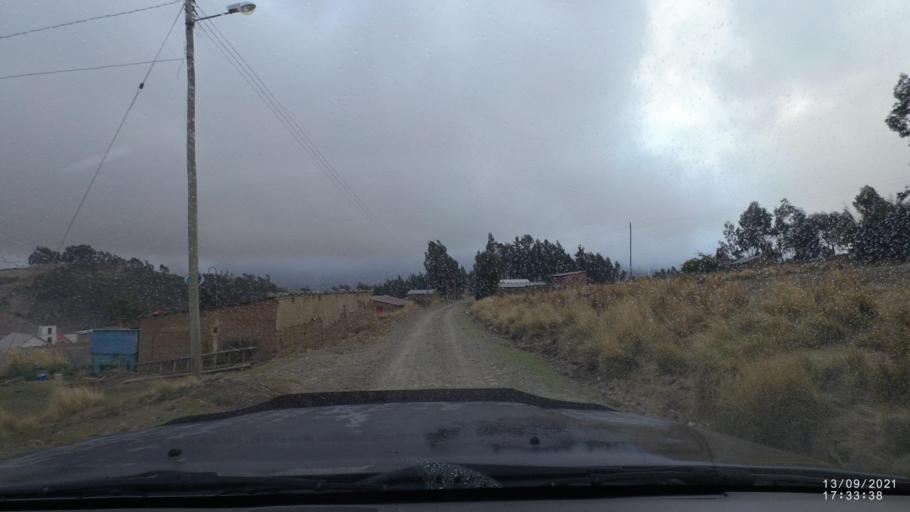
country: BO
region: Cochabamba
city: Colomi
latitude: -17.3667
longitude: -65.7925
